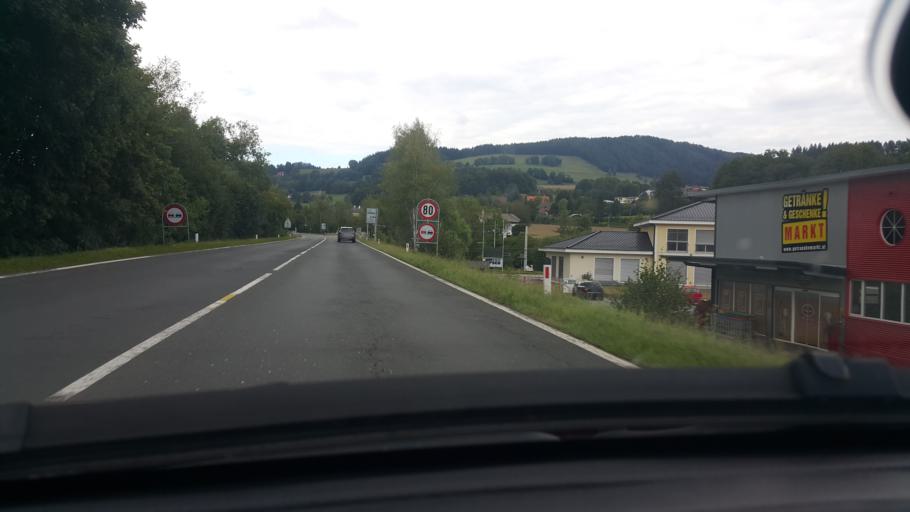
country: AT
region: Carinthia
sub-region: Politischer Bezirk Feldkirchen
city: Feldkirchen in Karnten
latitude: 46.7199
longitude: 14.1054
